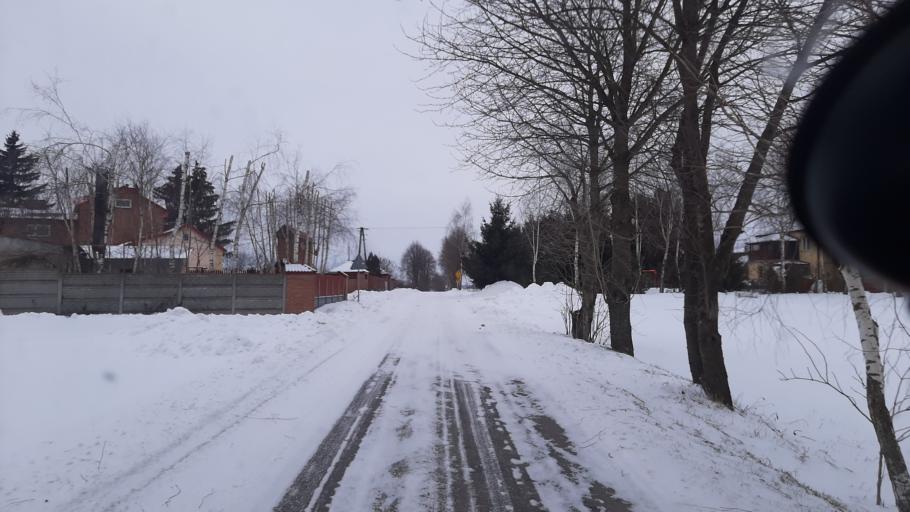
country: PL
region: Lublin Voivodeship
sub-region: Powiat lubelski
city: Garbow
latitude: 51.3299
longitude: 22.2996
